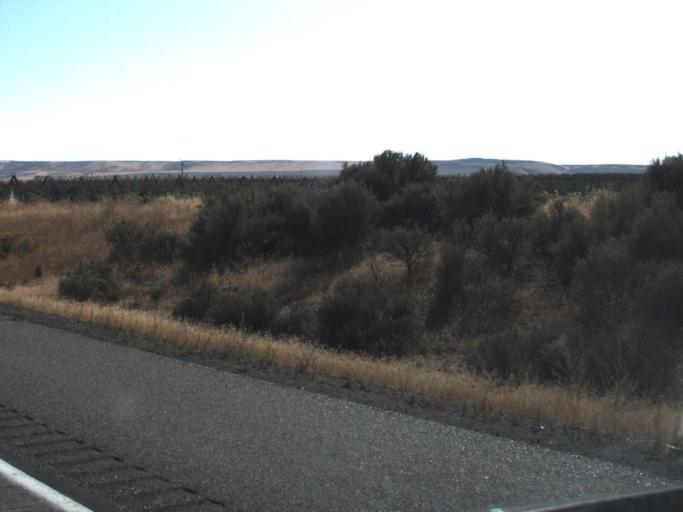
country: US
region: Washington
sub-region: Benton County
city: West Richland
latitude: 46.2323
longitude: -119.3564
